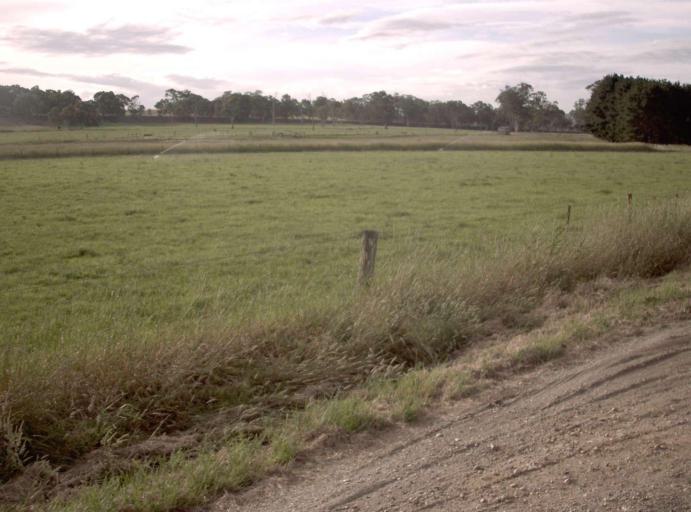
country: AU
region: Victoria
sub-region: Wellington
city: Sale
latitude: -37.9097
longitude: 146.9957
